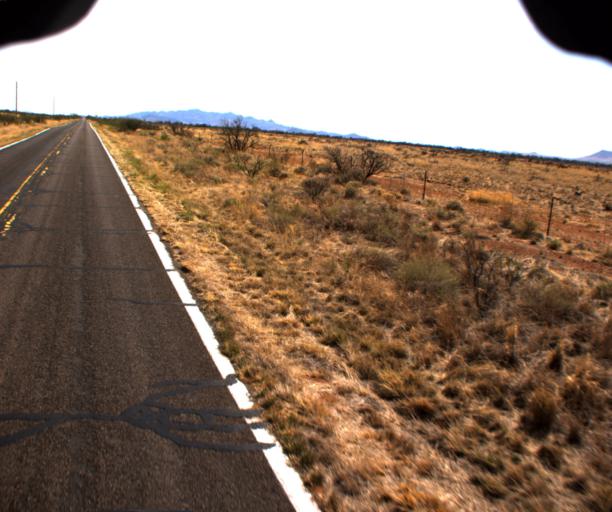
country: US
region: Arizona
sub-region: Cochise County
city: Willcox
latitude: 31.9044
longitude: -109.4914
